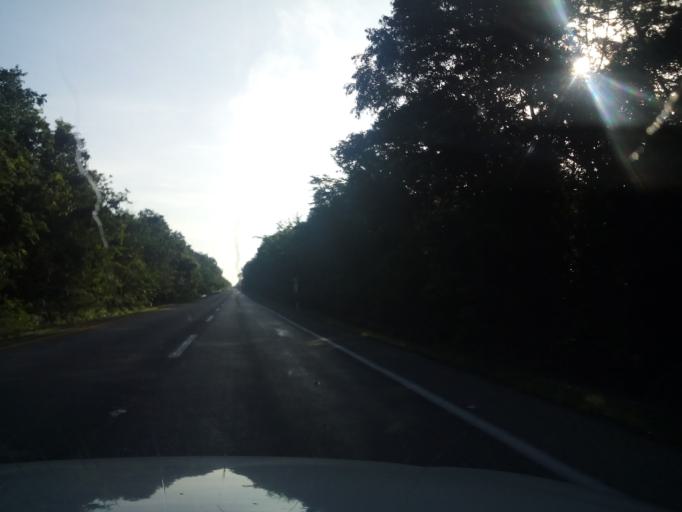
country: MX
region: Yucatan
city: Tinum
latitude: 20.7096
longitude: -88.4453
